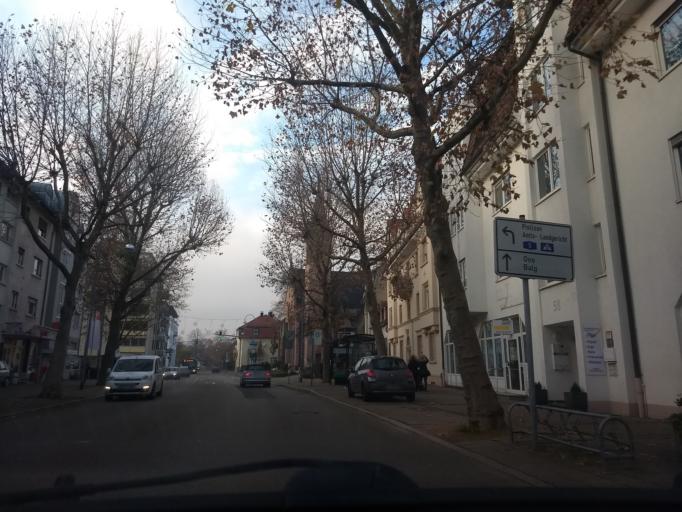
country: DE
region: Baden-Wuerttemberg
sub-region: Karlsruhe Region
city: Baden-Baden
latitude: 48.7778
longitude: 8.2183
